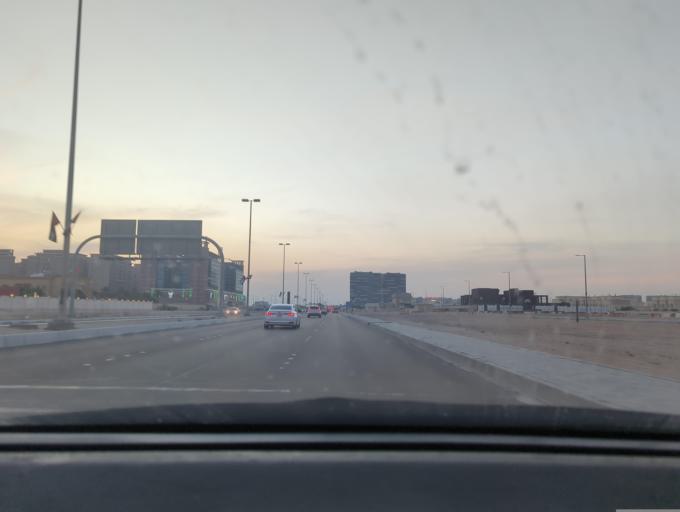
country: AE
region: Abu Dhabi
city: Abu Dhabi
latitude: 24.3747
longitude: 54.5436
